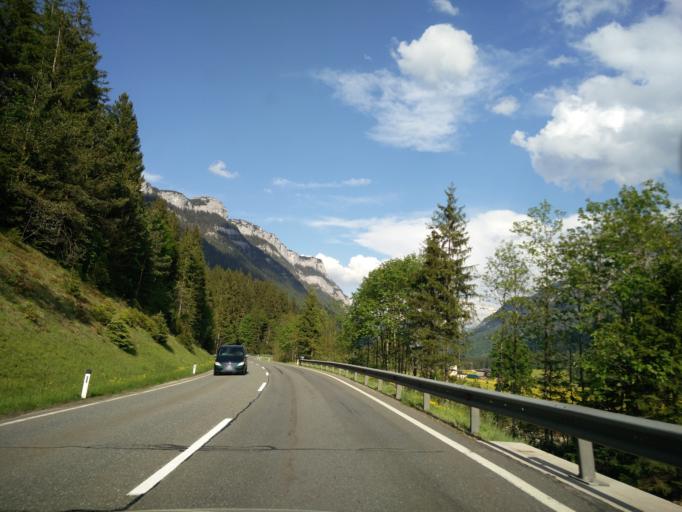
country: AT
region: Tyrol
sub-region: Politischer Bezirk Kitzbuhel
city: Waidring
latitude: 47.5875
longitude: 12.5903
